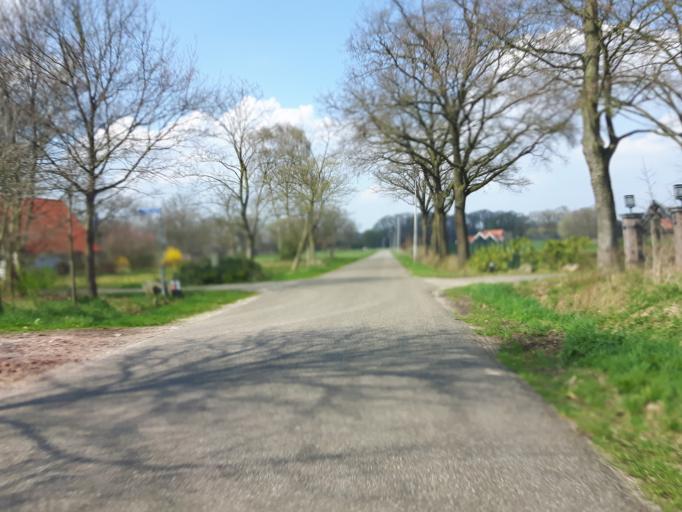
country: NL
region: Overijssel
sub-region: Gemeente Haaksbergen
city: Haaksbergen
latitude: 52.1956
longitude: 6.7960
